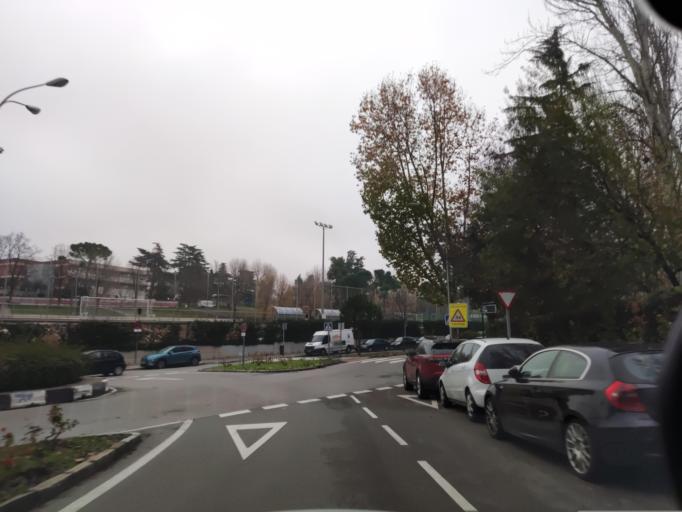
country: ES
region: Madrid
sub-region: Provincia de Madrid
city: Fuencarral-El Pardo
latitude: 40.4966
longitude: -3.7045
